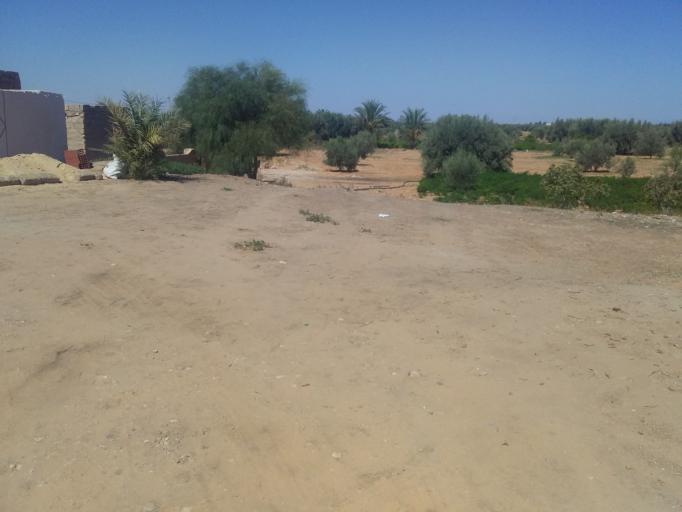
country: TN
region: Qabis
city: Matmata
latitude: 33.5835
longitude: 10.2797
